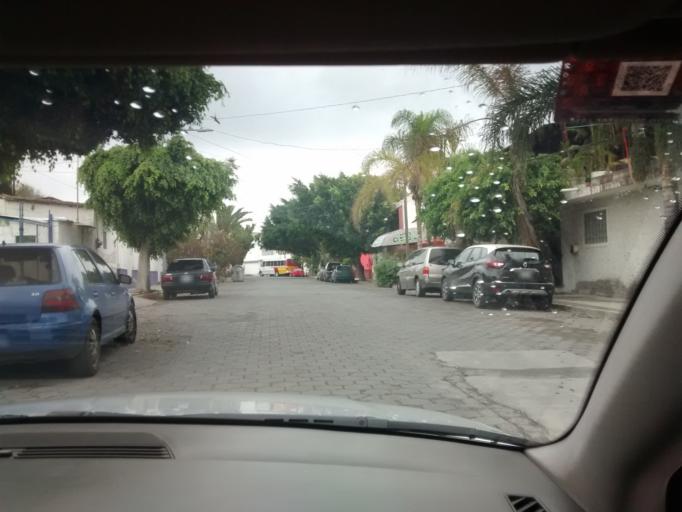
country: MX
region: Puebla
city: Tehuacan
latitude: 18.4590
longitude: -97.3990
